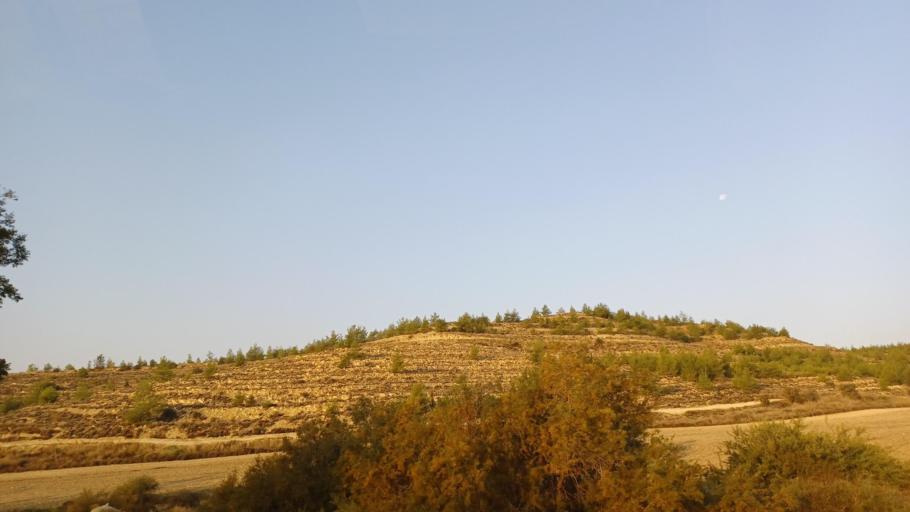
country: CY
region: Larnaka
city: Athienou
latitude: 35.0014
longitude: 33.5250
